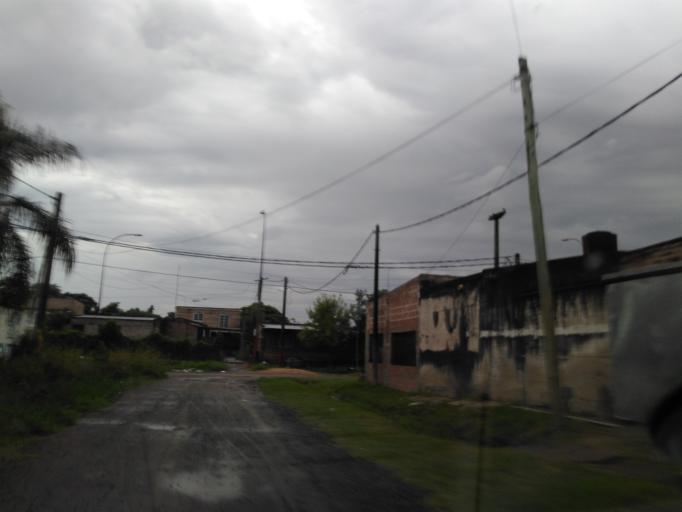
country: AR
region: Chaco
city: Resistencia
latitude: -27.4673
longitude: -58.9791
